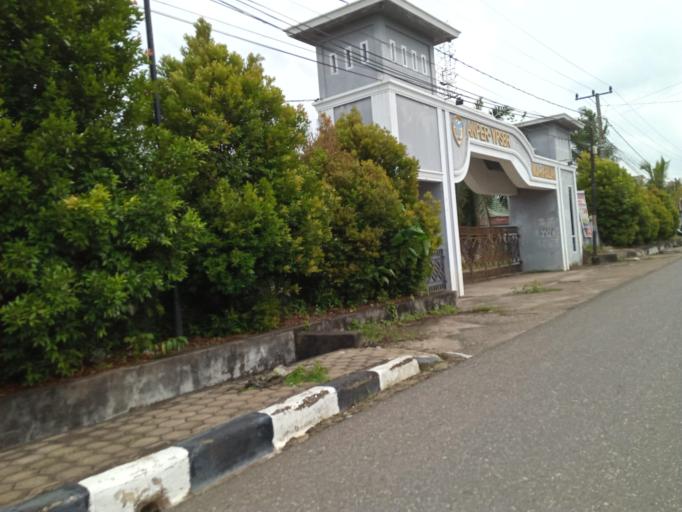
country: ID
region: Jambi
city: Muara Bulian
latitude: -1.7173
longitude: 103.2618
